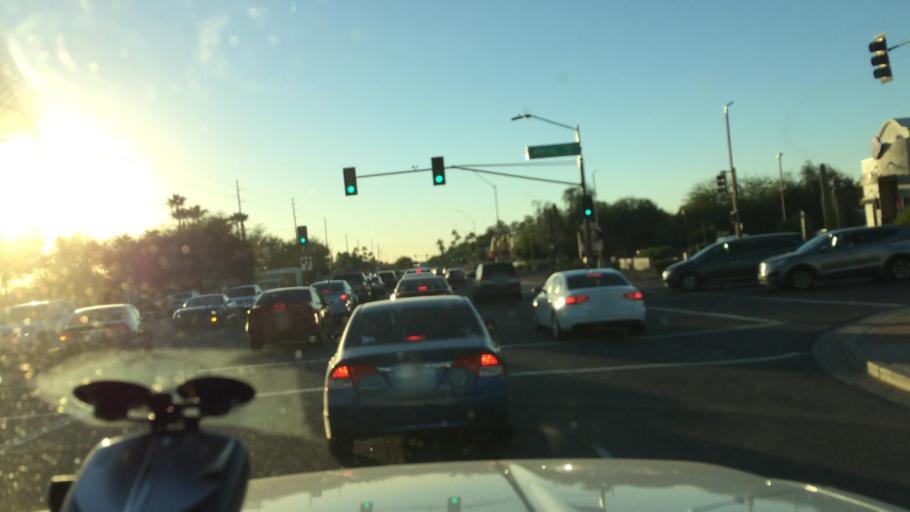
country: US
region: Arizona
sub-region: Maricopa County
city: Paradise Valley
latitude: 33.6402
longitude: -111.9748
